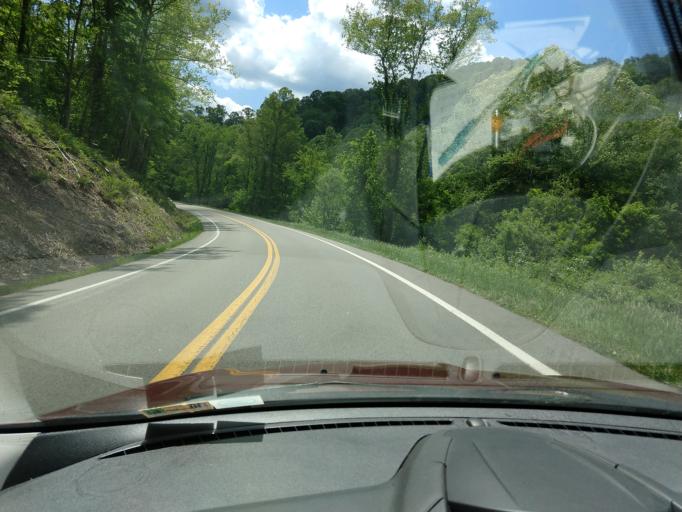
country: US
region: West Virginia
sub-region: Gilmer County
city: Glenville
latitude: 38.8841
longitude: -80.7220
